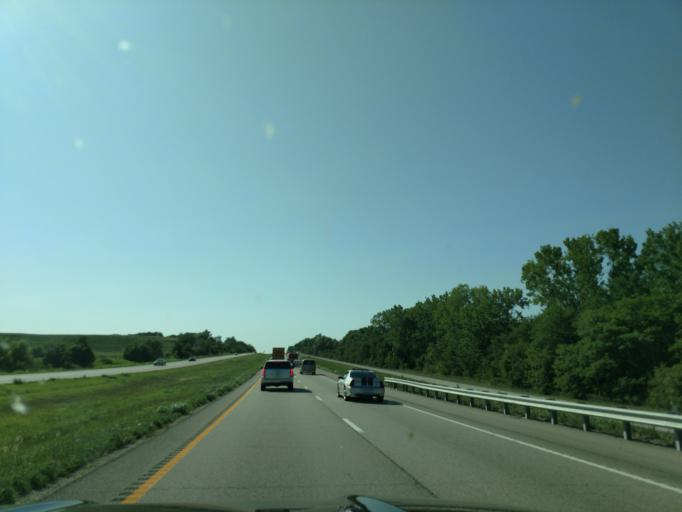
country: US
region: Missouri
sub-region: Andrew County
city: Country Club Village
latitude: 39.8735
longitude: -94.8356
